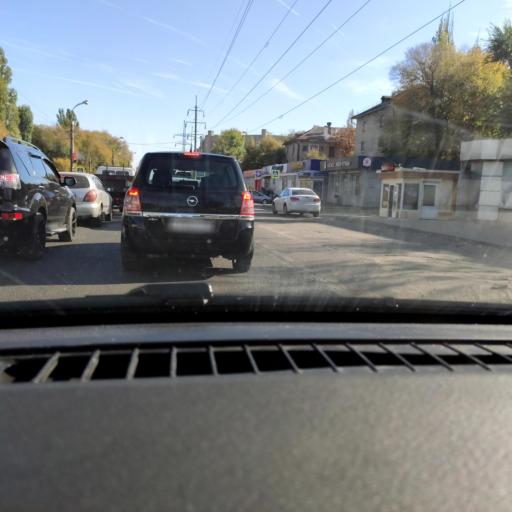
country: RU
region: Voronezj
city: Voronezh
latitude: 51.6416
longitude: 39.1572
